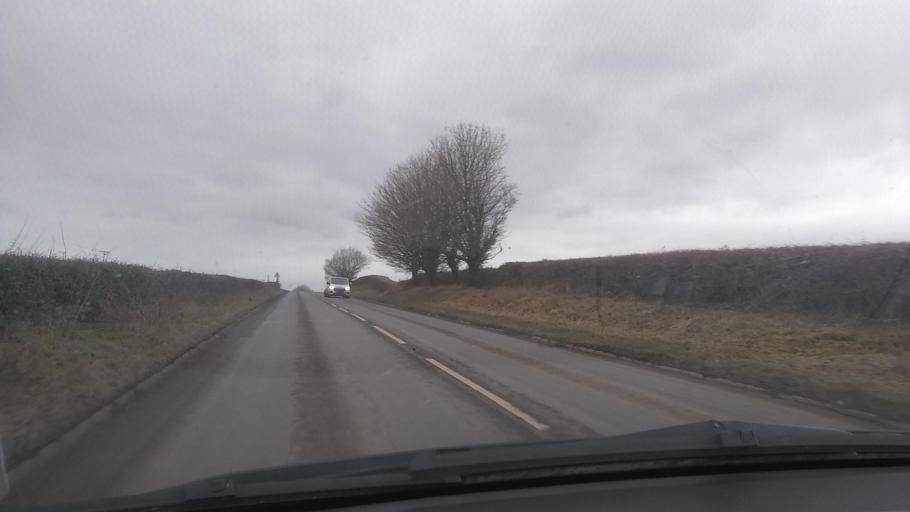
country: GB
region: England
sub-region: Shropshire
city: Cleobury Mortimer
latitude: 52.3763
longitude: -2.5037
